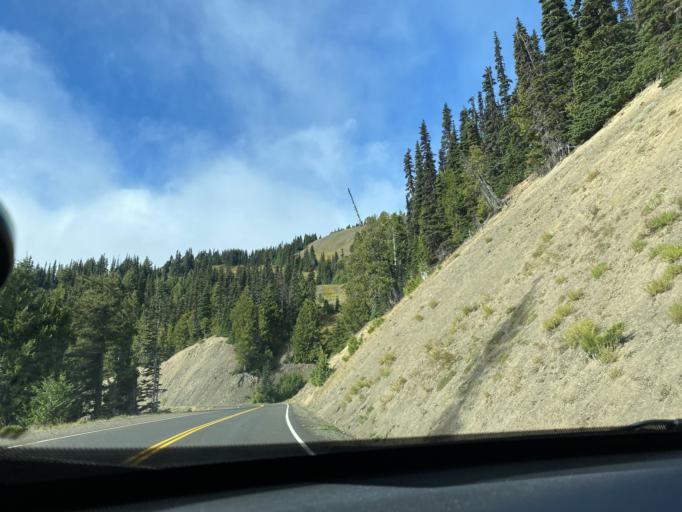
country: US
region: Washington
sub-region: Clallam County
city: Port Angeles
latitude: 47.9778
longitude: -123.4741
